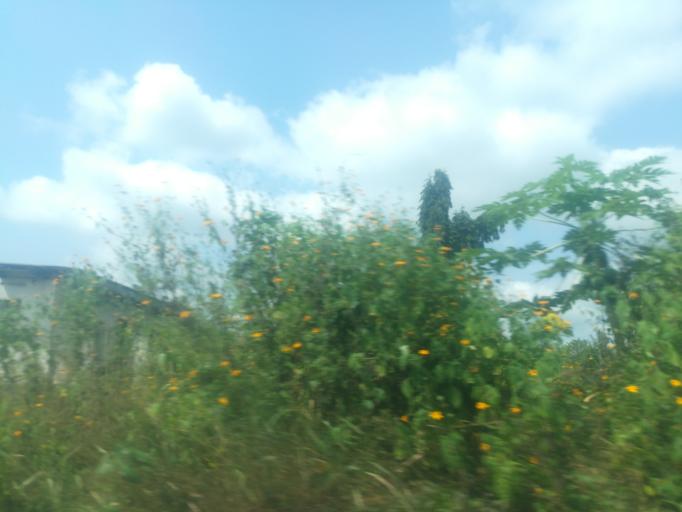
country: NG
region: Oyo
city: Moniya
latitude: 7.5559
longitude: 3.9098
